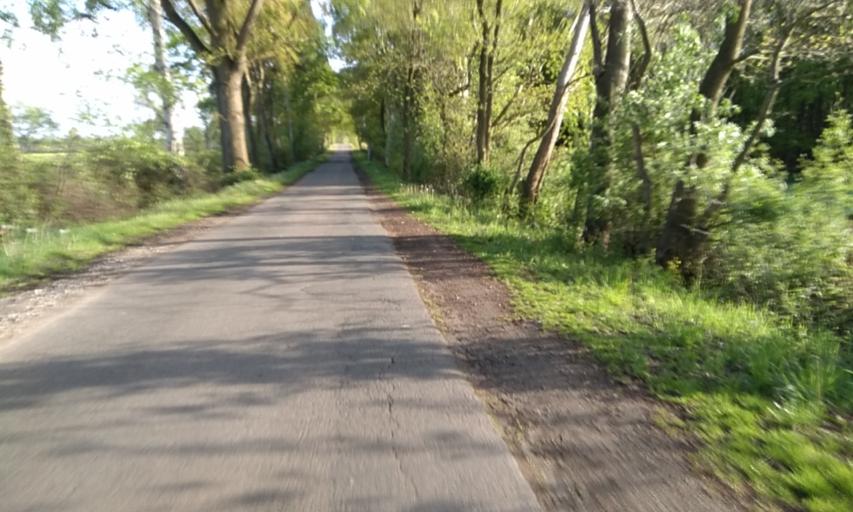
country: DE
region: Lower Saxony
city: Bliedersdorf
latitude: 53.4293
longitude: 9.5555
